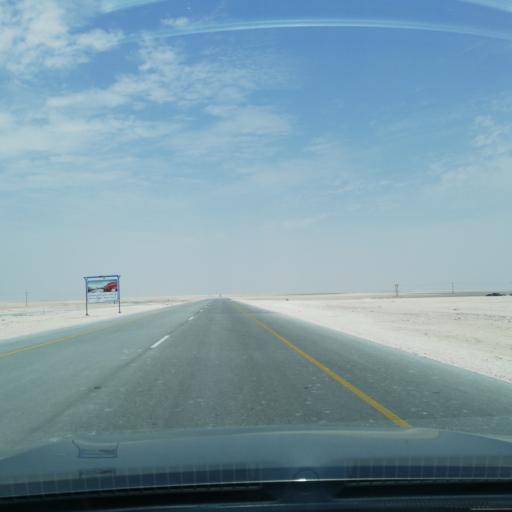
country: OM
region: Al Wusta
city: Hayma'
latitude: 19.6163
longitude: 55.7160
